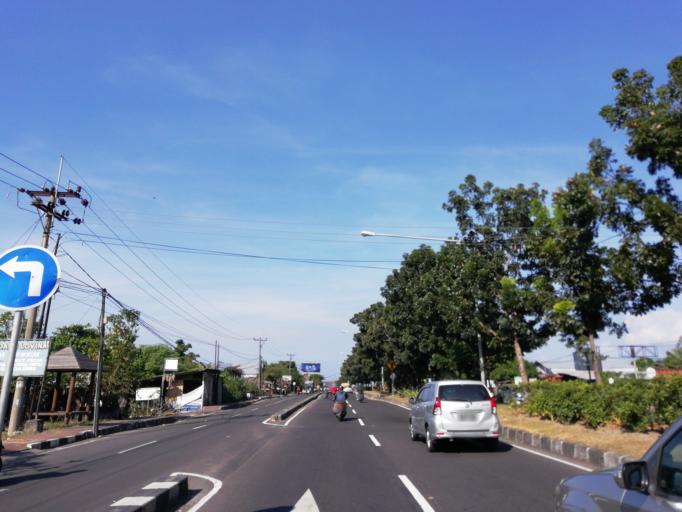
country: ID
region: Bali
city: Banjar Kertajiwa
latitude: -8.6486
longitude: 115.2670
